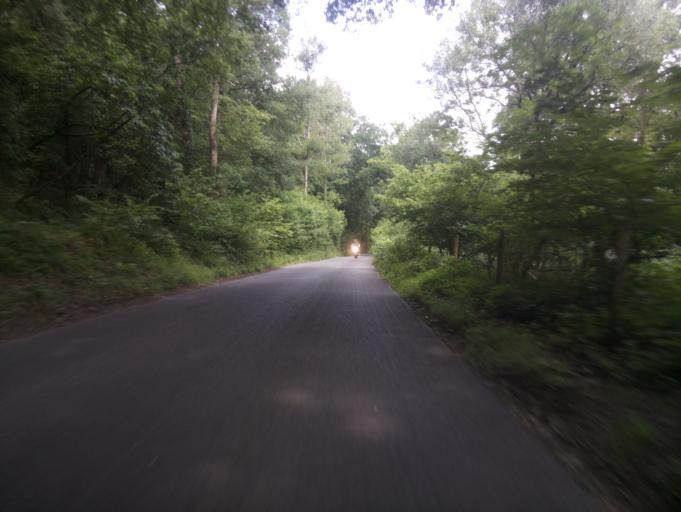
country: GB
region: England
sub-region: Gloucestershire
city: Bream
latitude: 51.7407
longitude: -2.5566
